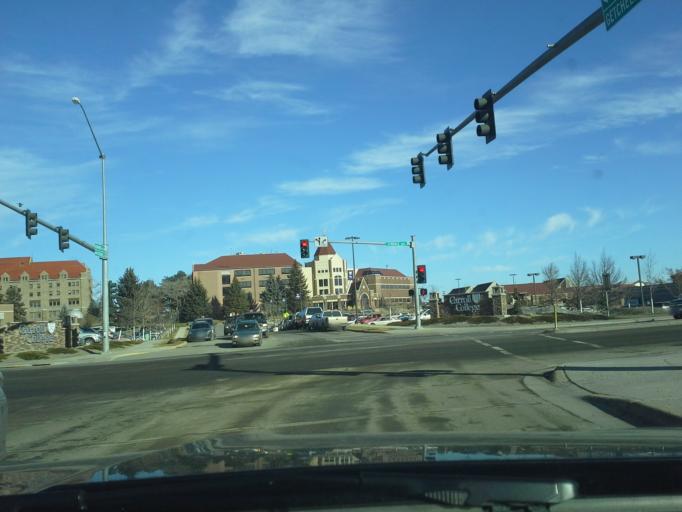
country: US
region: Montana
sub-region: Lewis and Clark County
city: Helena
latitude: 46.5978
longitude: -112.0378
